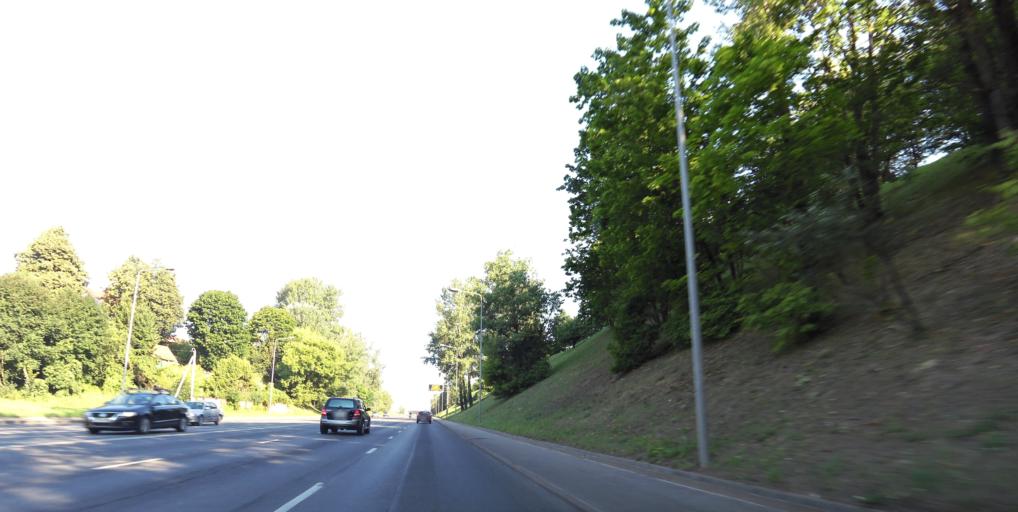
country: LT
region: Vilnius County
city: Seskine
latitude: 54.7052
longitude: 25.2563
